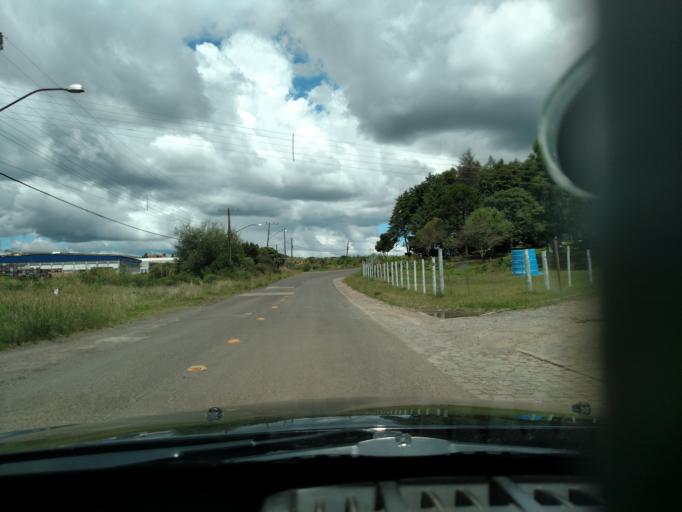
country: BR
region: Santa Catarina
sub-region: Sao Joaquim
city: Sao Joaquim
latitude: -28.2797
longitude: -49.9299
